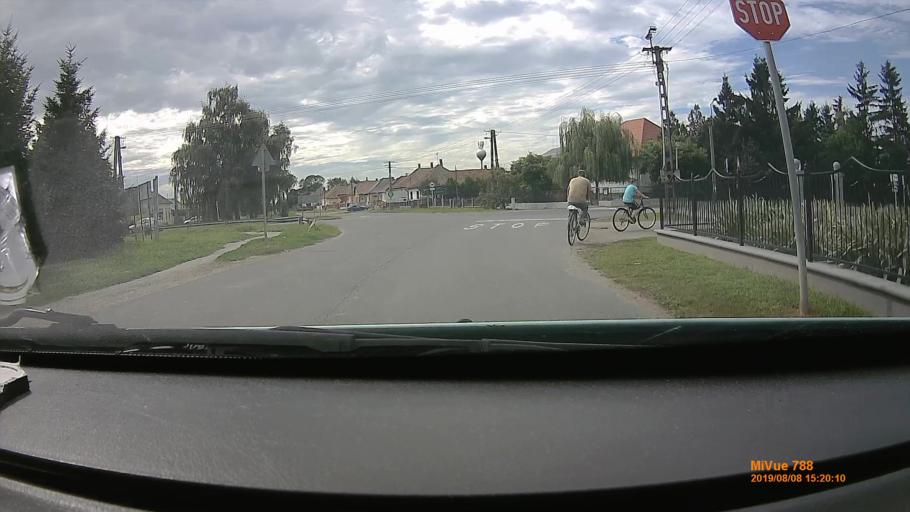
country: HU
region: Szabolcs-Szatmar-Bereg
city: Tunyogmatolcs
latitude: 47.9715
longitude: 22.4544
